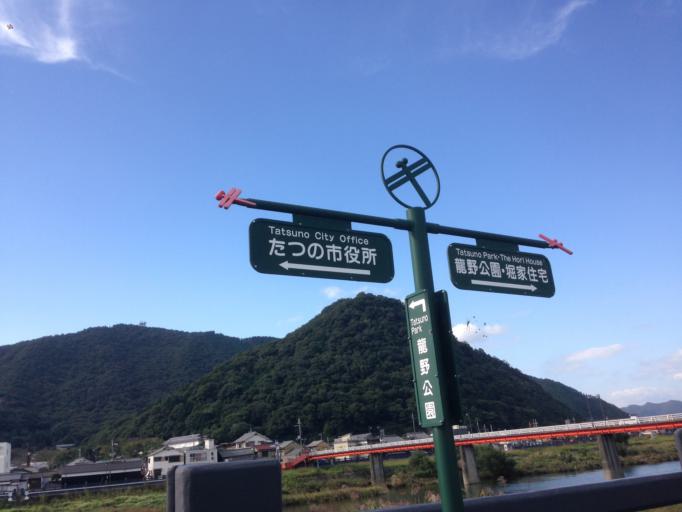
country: JP
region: Hyogo
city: Tatsunocho-tominaga
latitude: 34.8658
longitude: 134.5501
